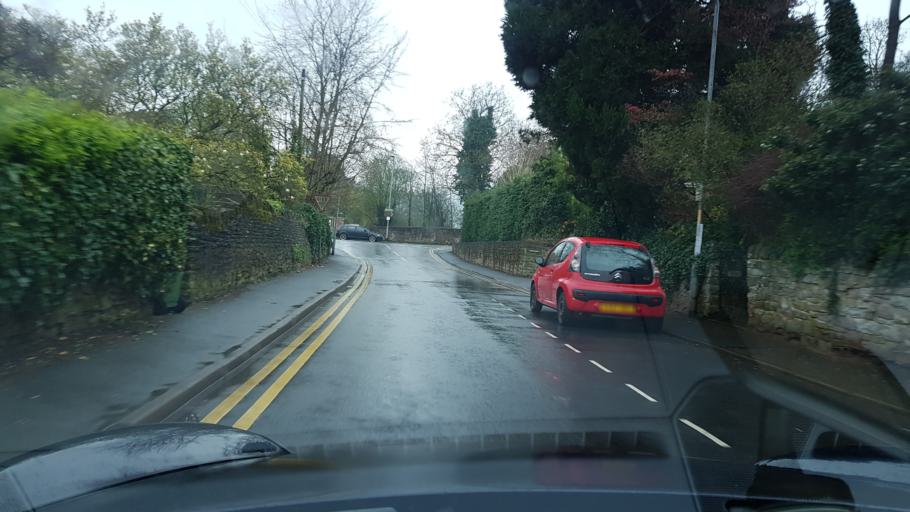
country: GB
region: England
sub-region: Herefordshire
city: Ross on Wye
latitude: 51.9143
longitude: -2.5781
